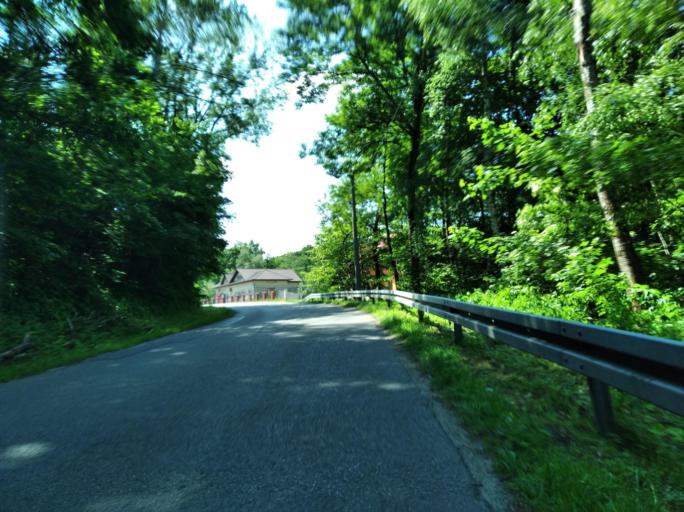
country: PL
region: Subcarpathian Voivodeship
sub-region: Powiat ropczycko-sedziszowski
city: Zagorzyce
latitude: 49.9870
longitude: 21.6455
